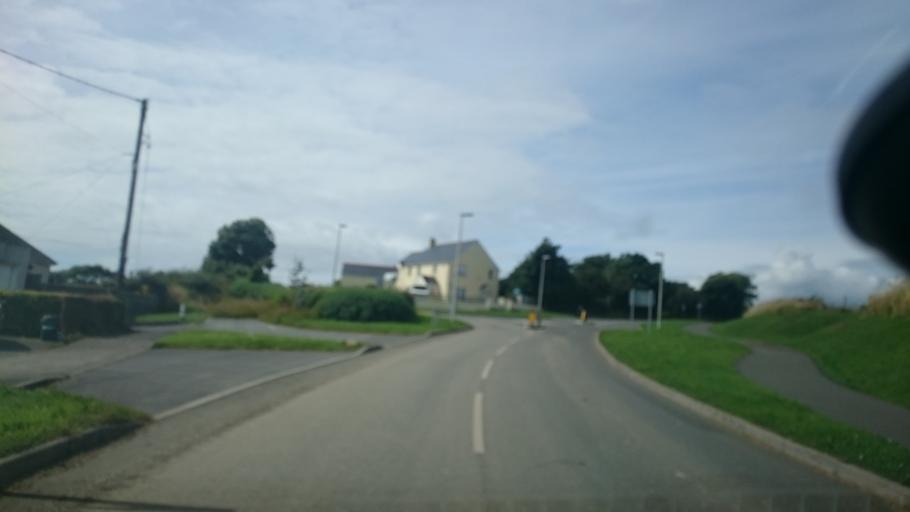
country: GB
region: Wales
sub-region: Pembrokeshire
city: Llangwm
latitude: 51.7505
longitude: -4.9181
